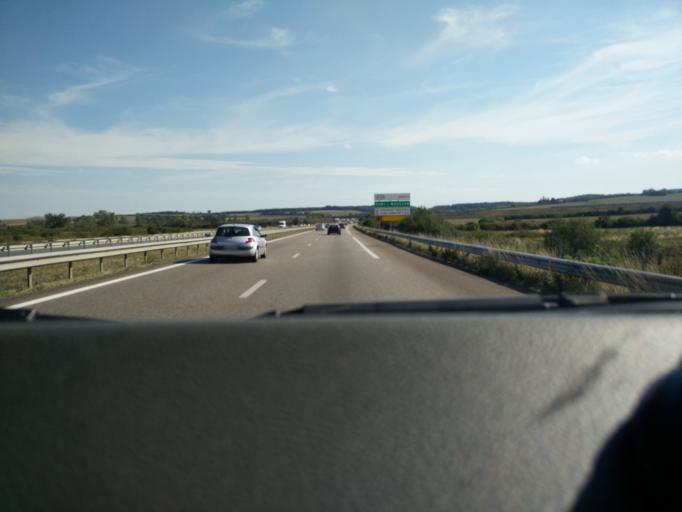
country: FR
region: Lorraine
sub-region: Departement de Meurthe-et-Moselle
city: Pont-a-Mousson
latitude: 48.9492
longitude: 6.1116
